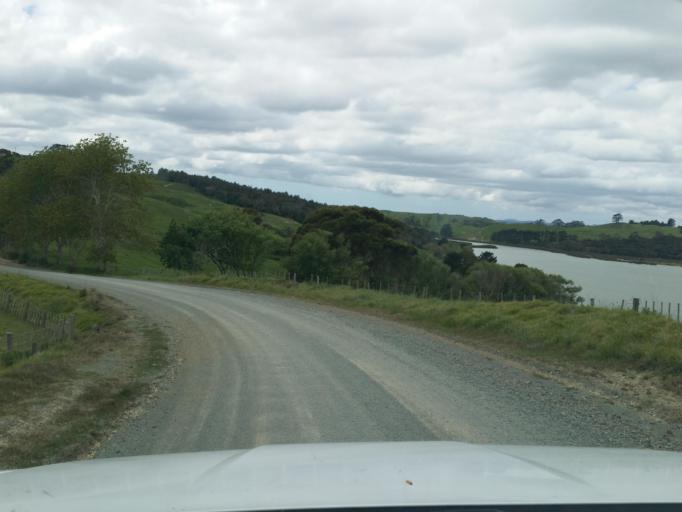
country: NZ
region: Auckland
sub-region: Auckland
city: Wellsford
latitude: -36.2756
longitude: 174.3695
